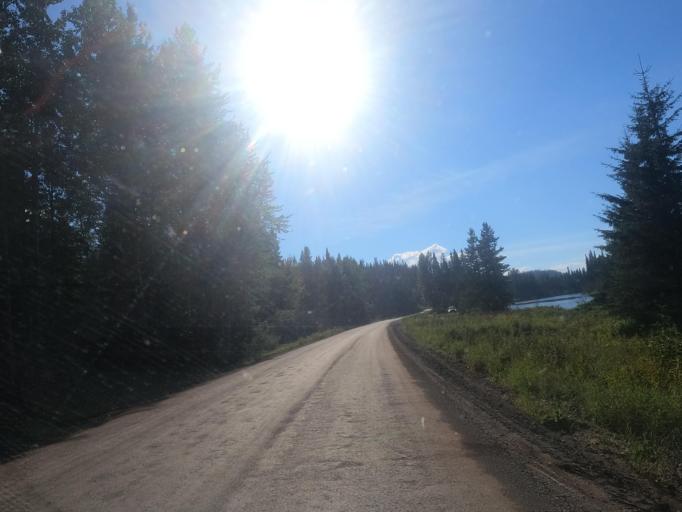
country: CA
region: British Columbia
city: Houston
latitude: 54.2016
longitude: -126.8605
